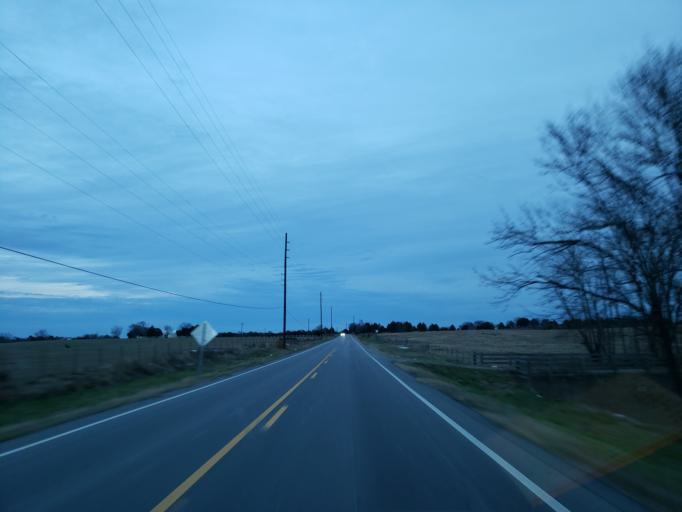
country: US
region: Alabama
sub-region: Sumter County
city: Livingston
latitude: 32.8124
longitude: -88.2764
